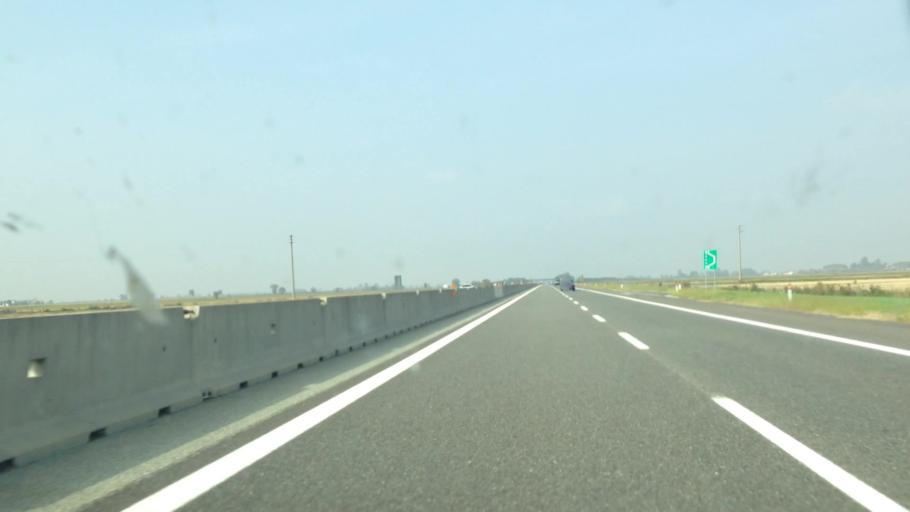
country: IT
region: Piedmont
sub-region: Provincia di Vercelli
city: Salasco
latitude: 45.3097
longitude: 8.2884
